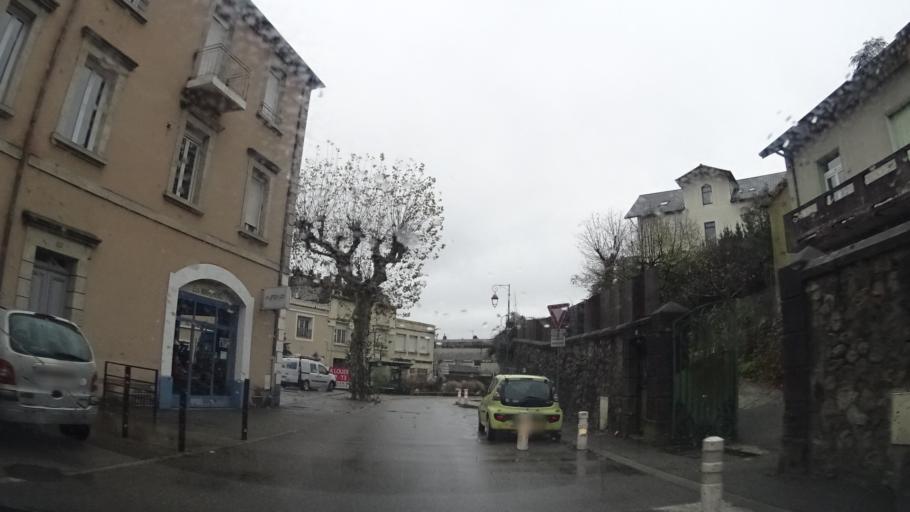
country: FR
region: Rhone-Alpes
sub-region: Departement de l'Ardeche
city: Labegude
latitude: 44.6537
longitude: 4.3651
